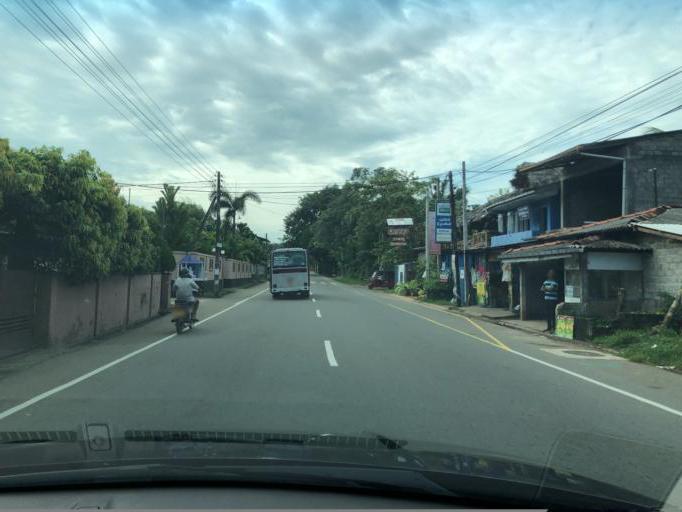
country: LK
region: Western
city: Kalutara
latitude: 6.5577
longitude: 80.0131
